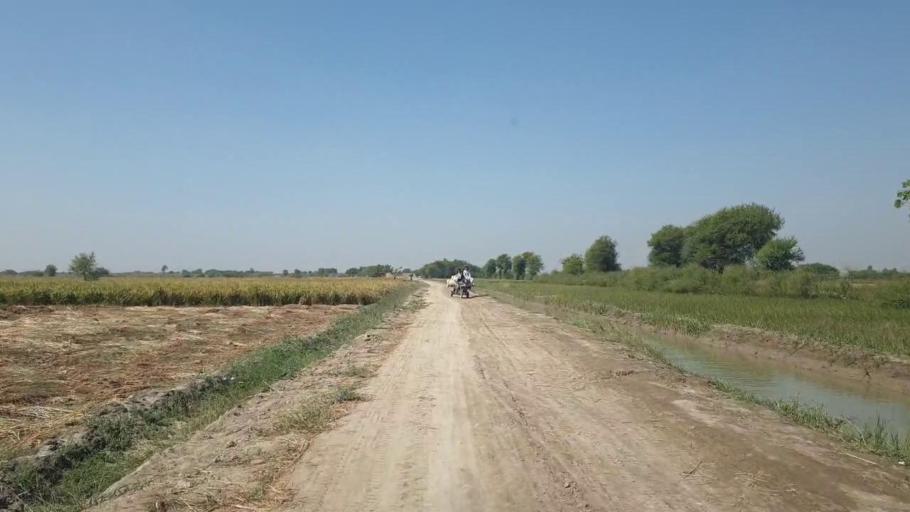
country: PK
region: Sindh
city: Talhar
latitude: 24.8054
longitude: 68.8058
